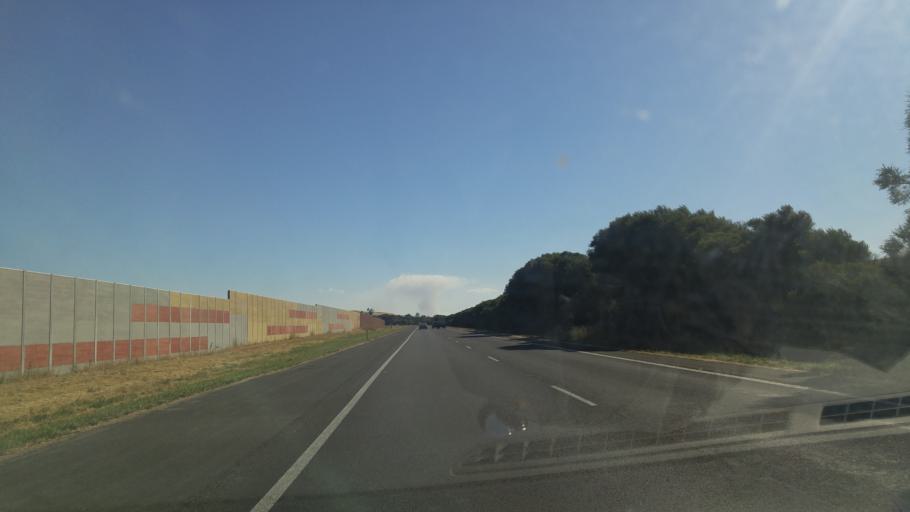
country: AU
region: Victoria
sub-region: Whittlesea
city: Whittlesea
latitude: -37.4242
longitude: 144.9891
